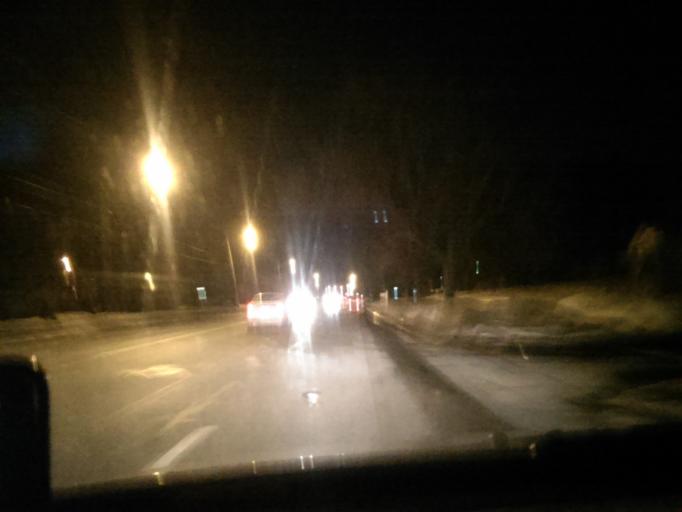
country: US
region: Massachusetts
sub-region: Hampden County
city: Ludlow
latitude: 42.1222
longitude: -72.4977
